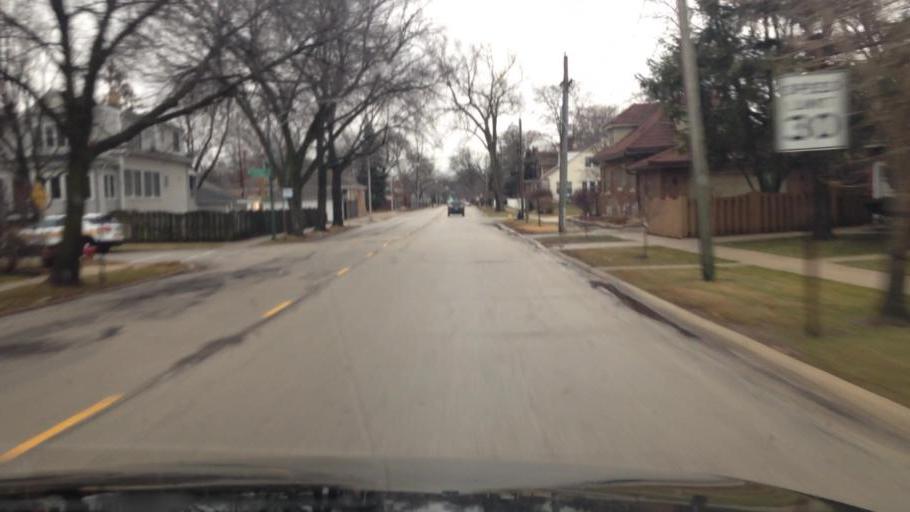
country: US
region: Illinois
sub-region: Cook County
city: Park Ridge
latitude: 42.0032
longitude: -87.8215
